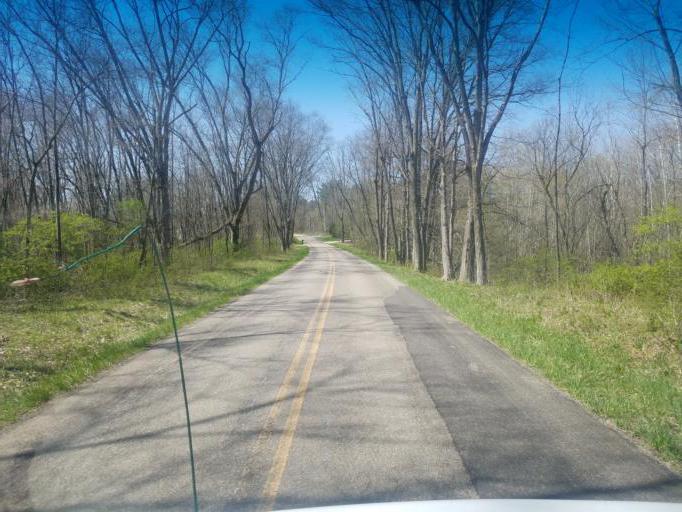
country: US
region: Ohio
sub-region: Knox County
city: Oak Hill
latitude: 40.3912
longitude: -82.2703
